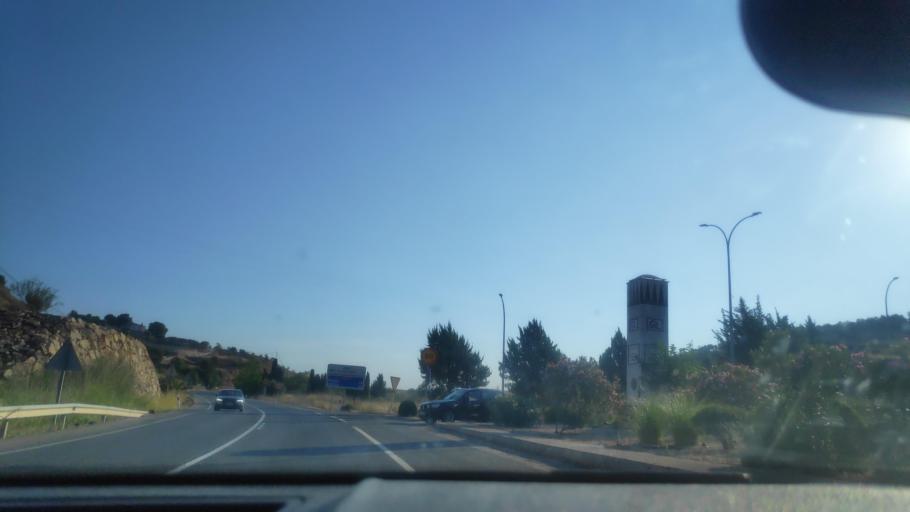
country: ES
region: Andalusia
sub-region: Provincia de Jaen
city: La Guardia de Jaen
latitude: 37.7792
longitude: -3.7323
